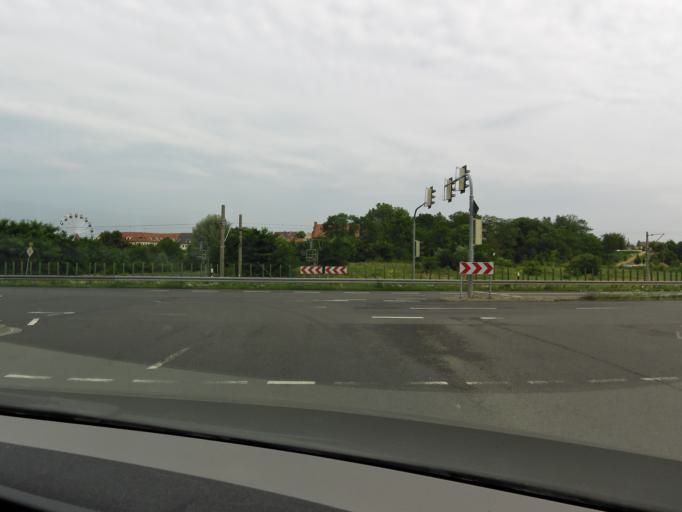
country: DE
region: Saxony-Anhalt
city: Wittenburg
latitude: 51.8614
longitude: 12.6524
